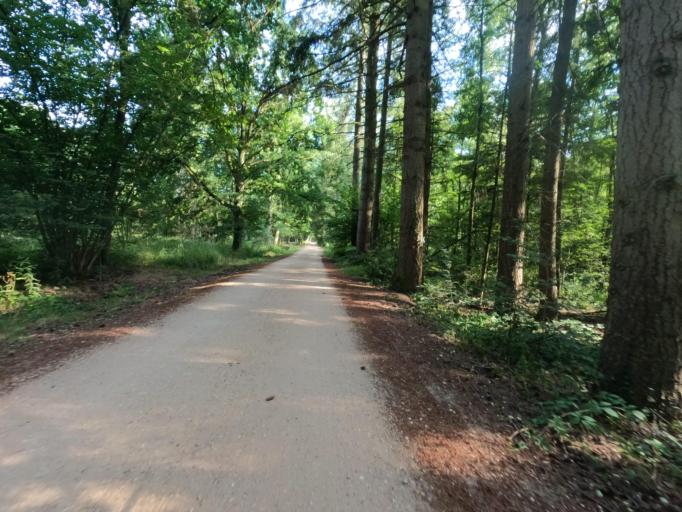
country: NL
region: Limburg
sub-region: Gemeente Beesel
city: Offenbeek
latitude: 51.2289
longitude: 6.0884
